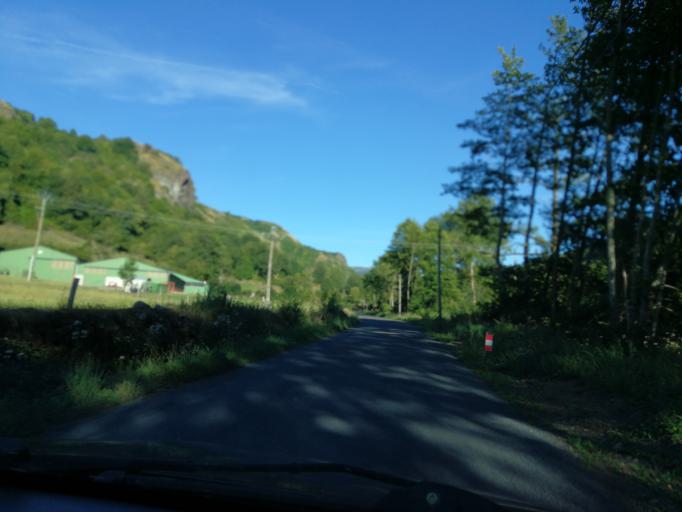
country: FR
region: Auvergne
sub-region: Departement du Cantal
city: Saint-Cernin
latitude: 45.1083
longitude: 2.5138
